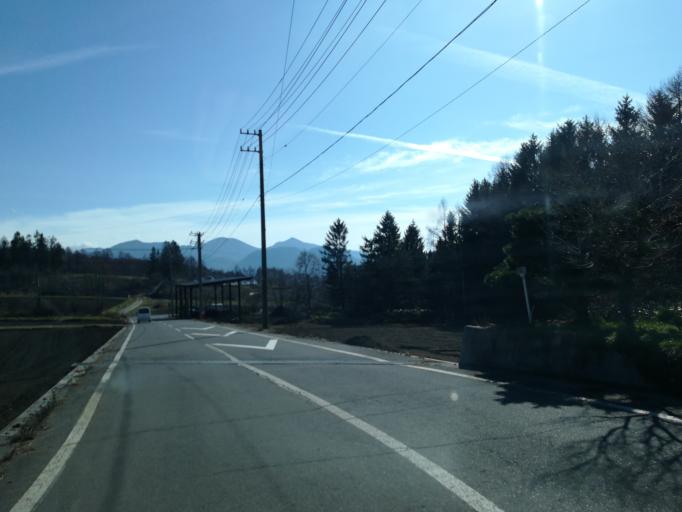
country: JP
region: Nagano
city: Ueda
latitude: 36.5197
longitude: 138.3413
